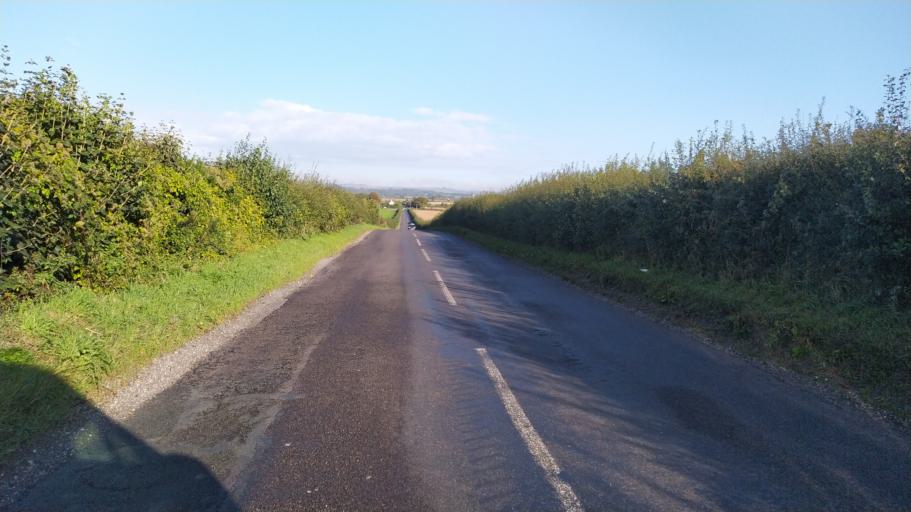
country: GB
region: England
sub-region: Wiltshire
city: Bower Chalke
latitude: 50.9114
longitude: -2.0451
